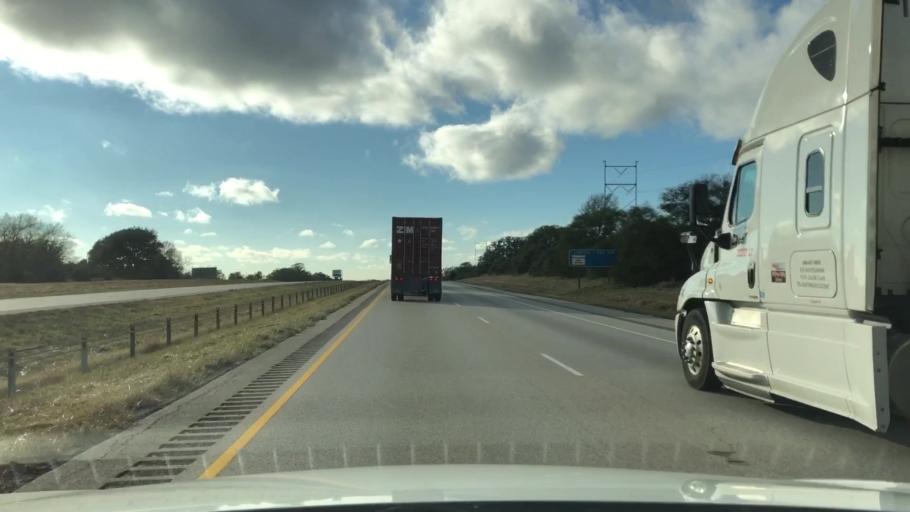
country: US
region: Texas
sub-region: Colorado County
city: Columbus
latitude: 29.6928
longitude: -96.6298
